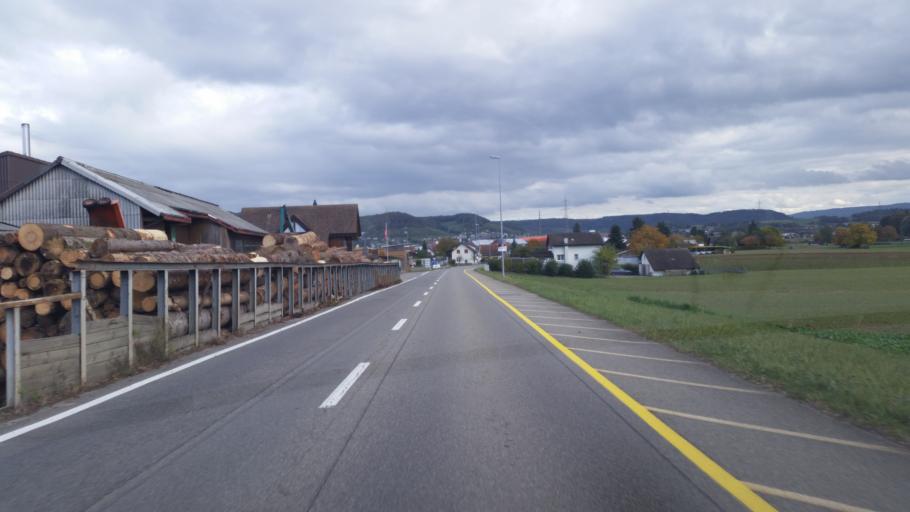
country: CH
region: Aargau
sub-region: Bezirk Zurzach
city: Klingnau
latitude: 47.5784
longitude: 8.2225
